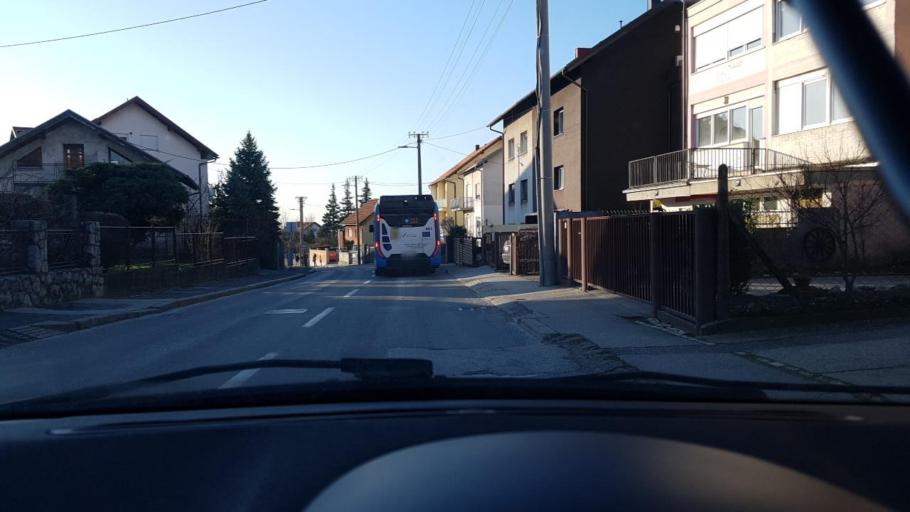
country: HR
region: Grad Zagreb
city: Zagreb
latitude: 45.8408
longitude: 16.0015
